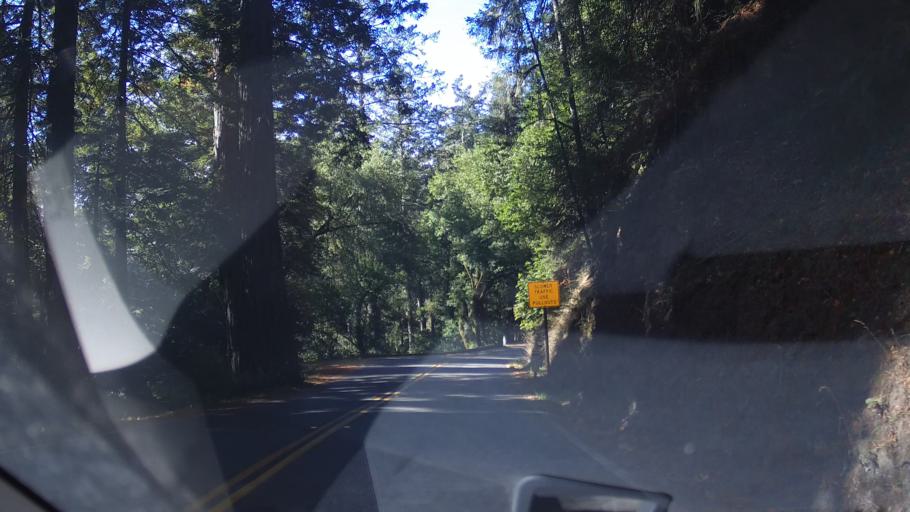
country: US
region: California
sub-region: Marin County
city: Mill Valley
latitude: 37.8995
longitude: -122.6116
